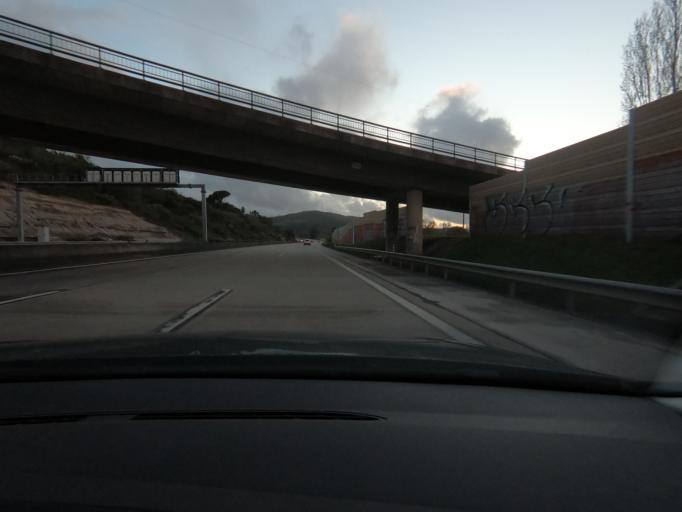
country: PT
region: Lisbon
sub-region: Loures
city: Bucelas
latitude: 38.9001
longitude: -9.1053
